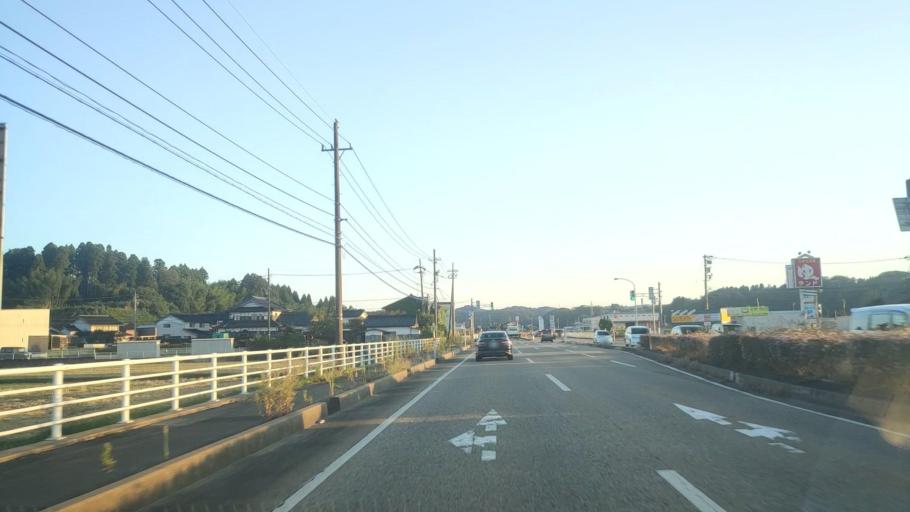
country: JP
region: Toyama
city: Himi
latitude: 36.8217
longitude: 136.9950
